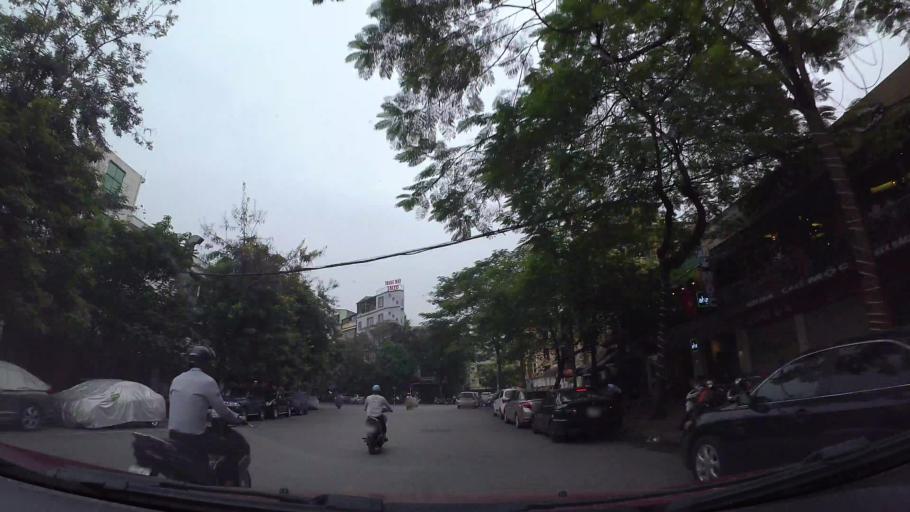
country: VN
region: Ha Noi
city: Hai BaTrung
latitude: 21.0058
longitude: 105.8457
